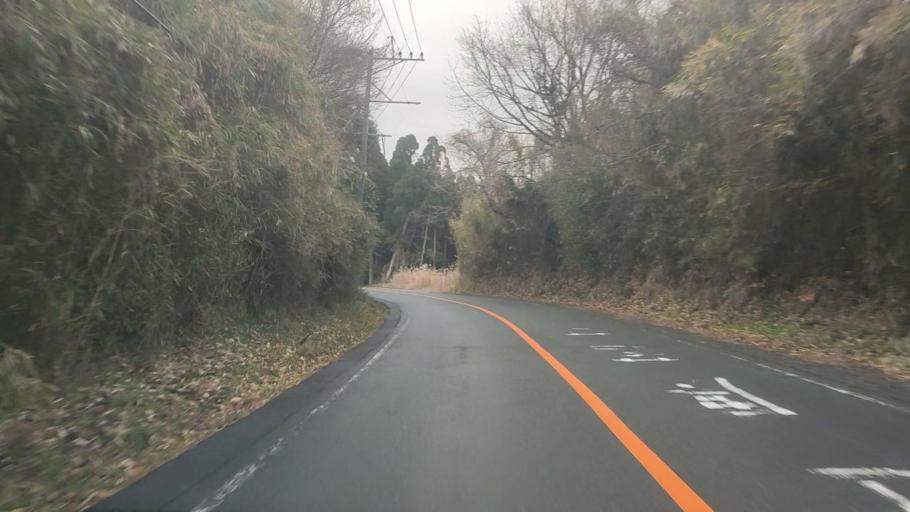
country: JP
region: Kumamoto
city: Aso
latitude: 32.8940
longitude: 131.0190
